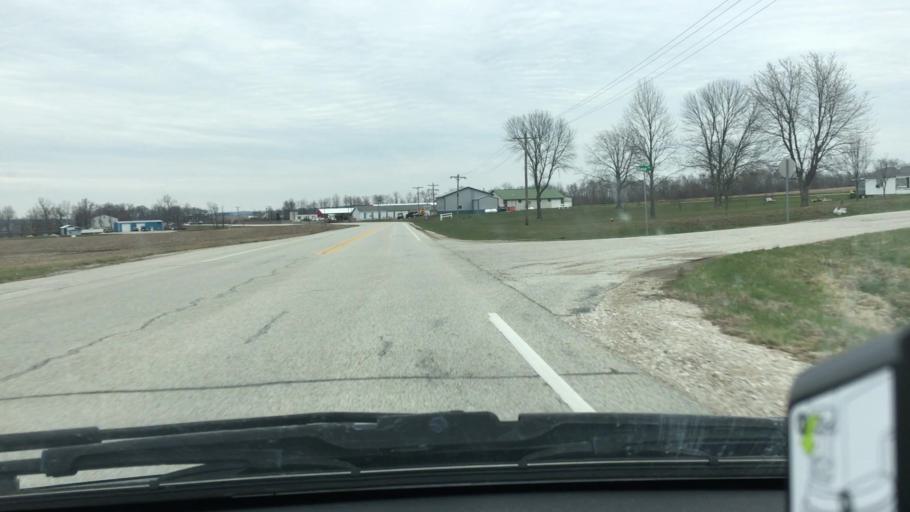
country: US
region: Indiana
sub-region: Greene County
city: Bloomfield
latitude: 39.0237
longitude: -87.0130
